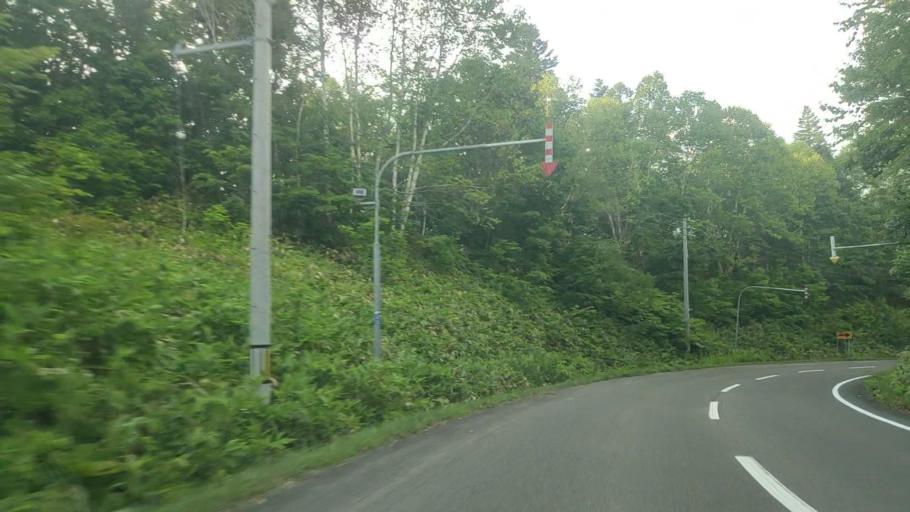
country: JP
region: Hokkaido
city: Bibai
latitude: 43.1746
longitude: 142.0683
